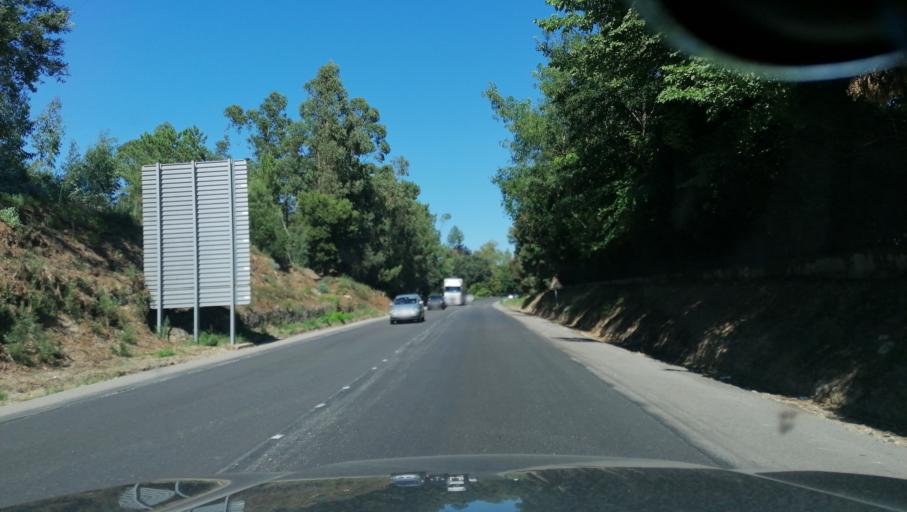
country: PT
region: Aveiro
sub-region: Santa Maria da Feira
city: Feira
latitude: 40.9319
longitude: -8.5470
